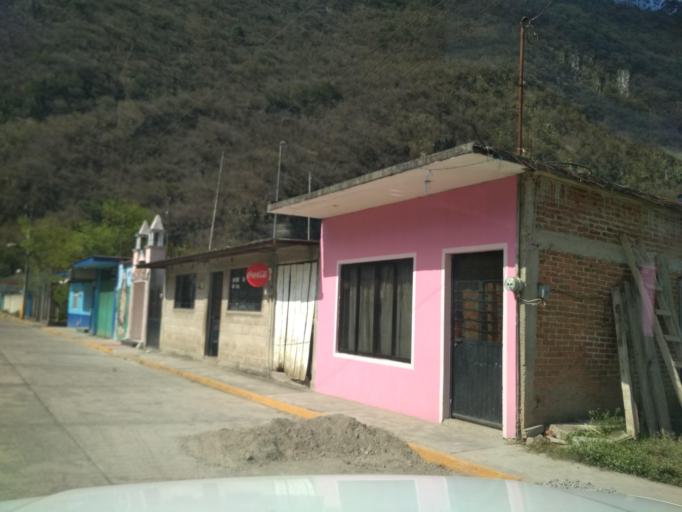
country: MX
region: Veracruz
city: Jalapilla
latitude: 18.8080
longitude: -97.0978
